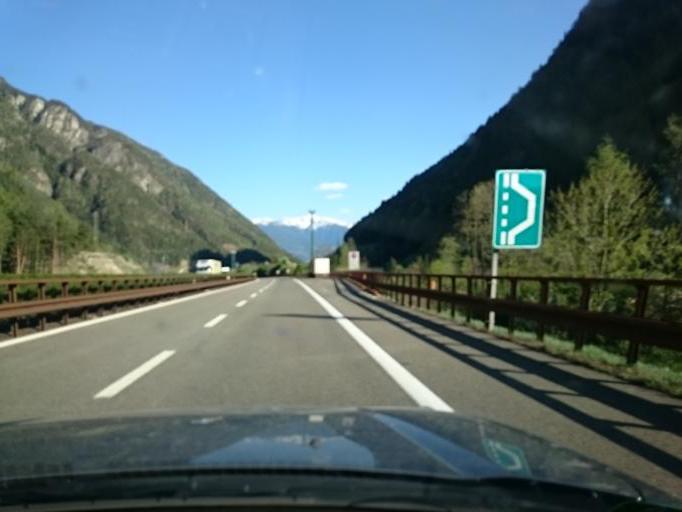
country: IT
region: Trentino-Alto Adige
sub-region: Bolzano
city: Fortezza
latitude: 46.8000
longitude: 11.5968
